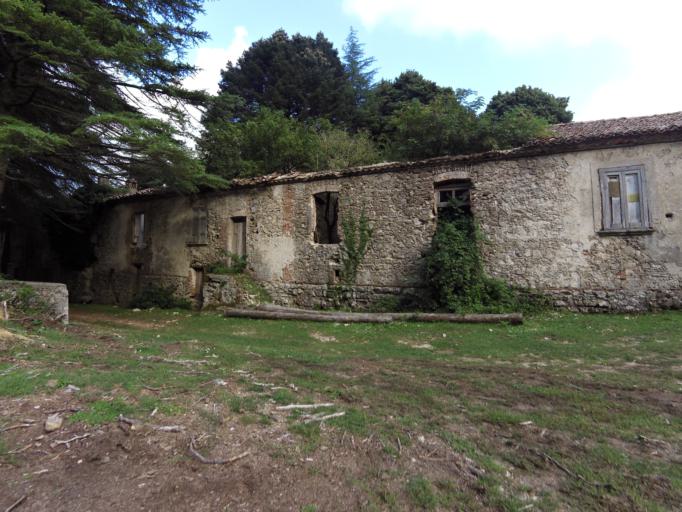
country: IT
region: Calabria
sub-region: Provincia di Vibo-Valentia
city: Nardodipace
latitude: 38.5086
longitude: 16.3794
